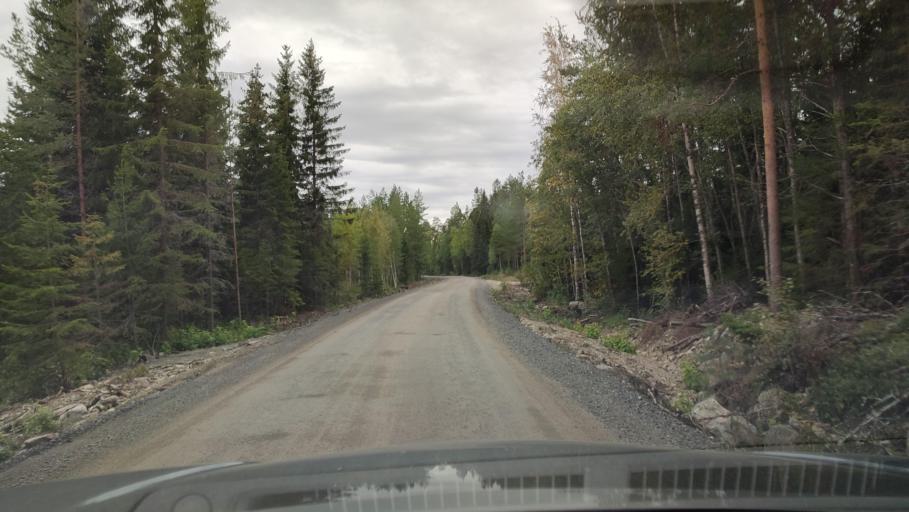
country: FI
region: Southern Ostrobothnia
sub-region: Suupohja
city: Karijoki
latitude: 62.1977
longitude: 21.5899
